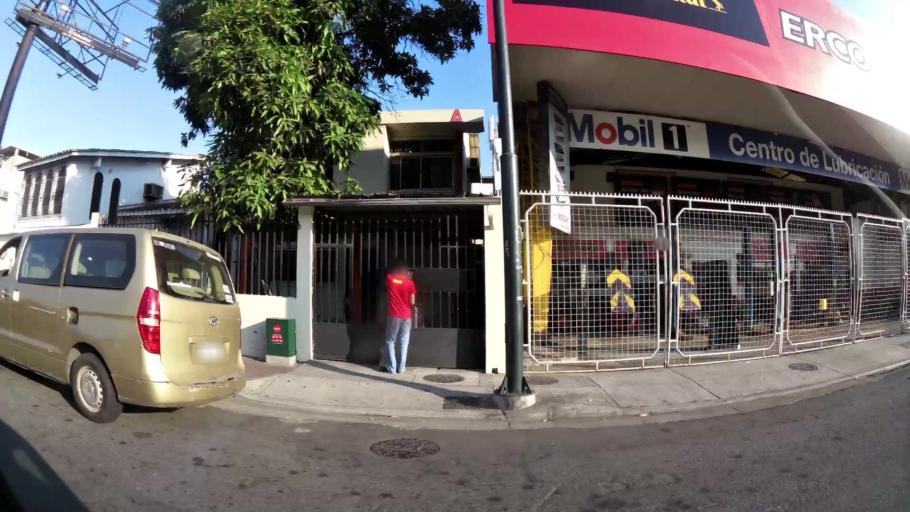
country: EC
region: Guayas
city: Guayaquil
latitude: -2.1714
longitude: -79.8980
